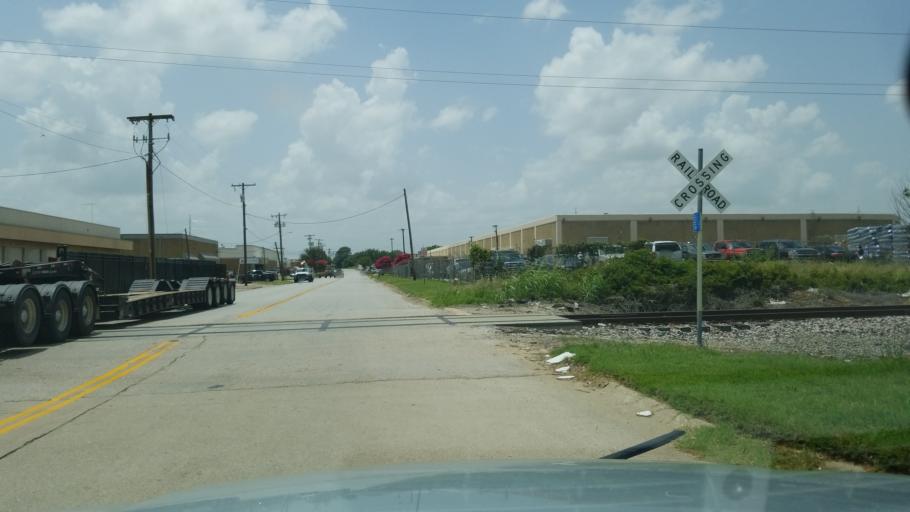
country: US
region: Texas
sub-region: Dallas County
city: Irving
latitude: 32.8184
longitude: -96.9120
